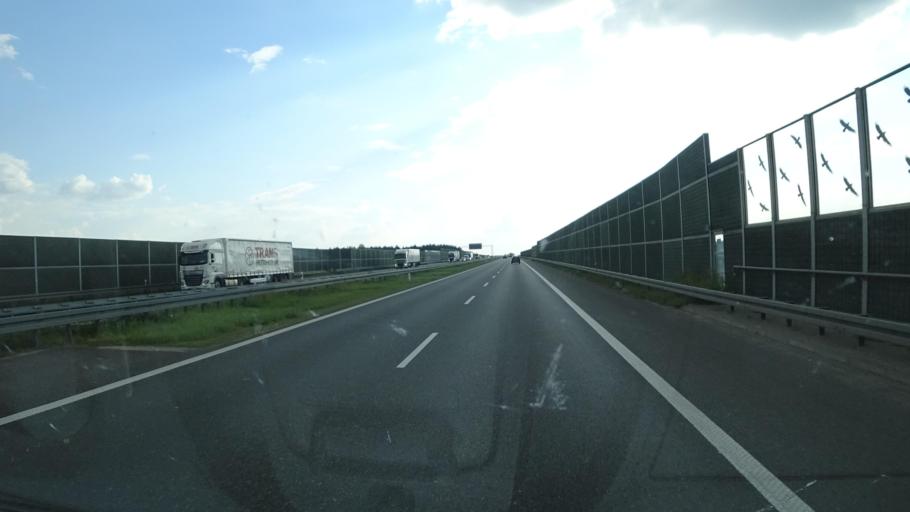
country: PL
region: Lodz Voivodeship
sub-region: powiat Lowicki
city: Bobrowniki
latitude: 52.0409
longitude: 20.0340
